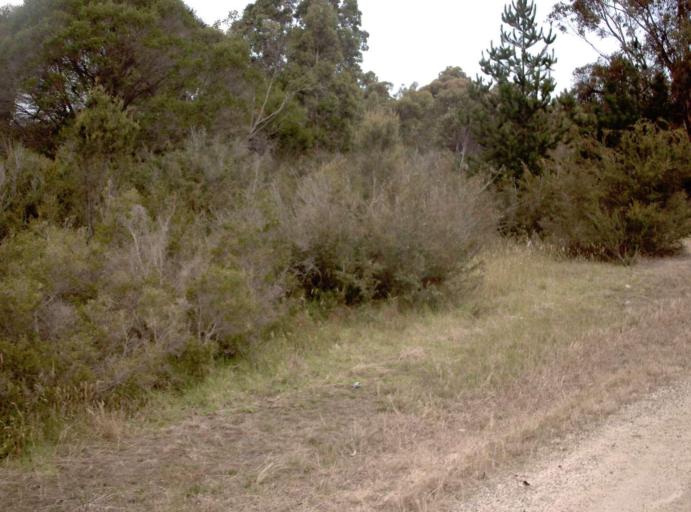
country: AU
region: Victoria
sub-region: Wellington
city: Sale
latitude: -38.1975
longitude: 147.0956
